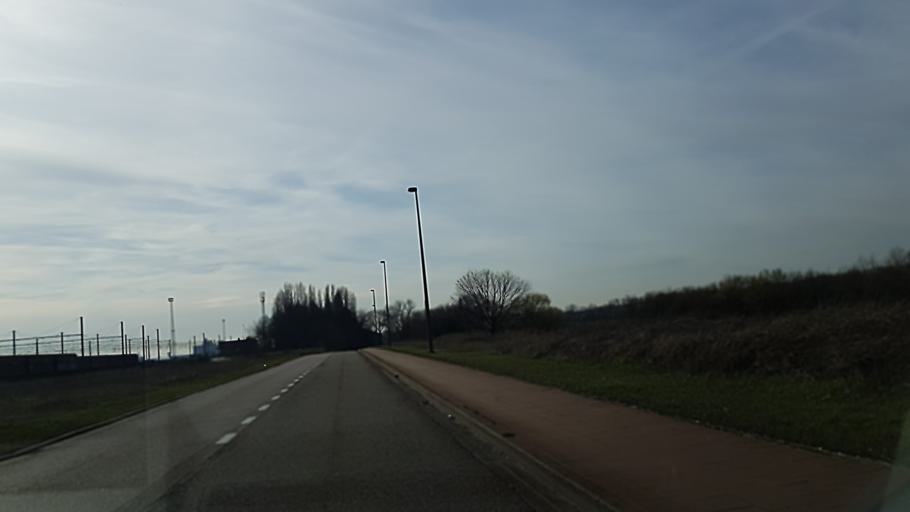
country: BE
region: Flanders
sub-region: Provincie Antwerpen
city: Stabroek
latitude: 51.3347
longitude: 4.3284
